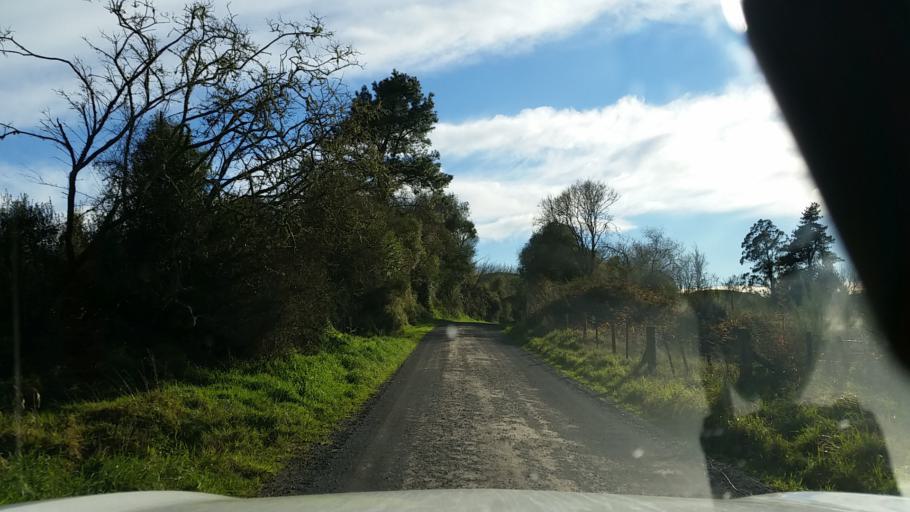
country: NZ
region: Waikato
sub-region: South Waikato District
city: Tokoroa
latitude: -38.3869
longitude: 176.0781
